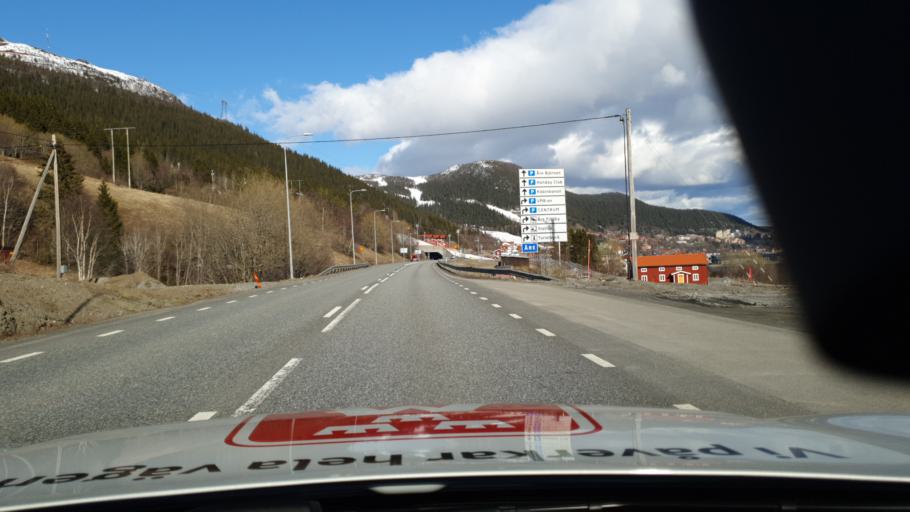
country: SE
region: Jaemtland
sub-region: Are Kommun
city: Are
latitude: 63.4060
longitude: 13.0480
